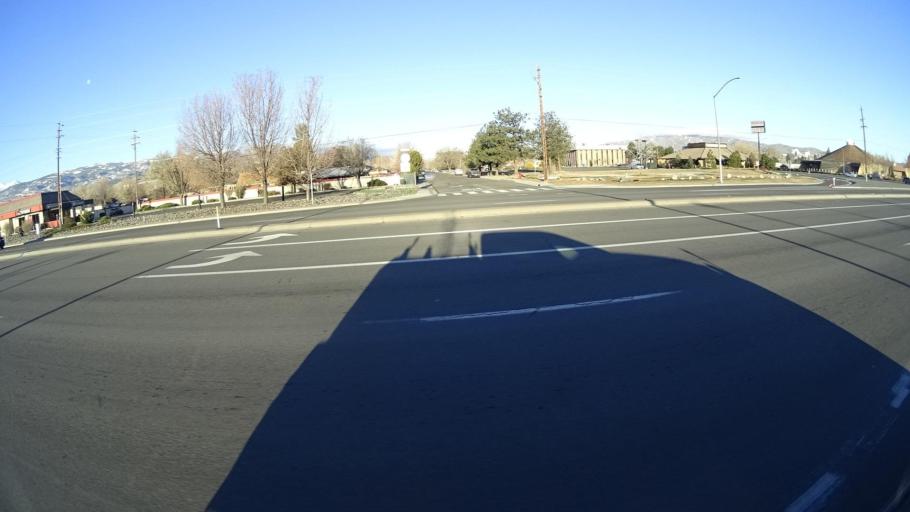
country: US
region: Nevada
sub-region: Washoe County
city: Reno
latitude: 39.5047
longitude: -119.7890
